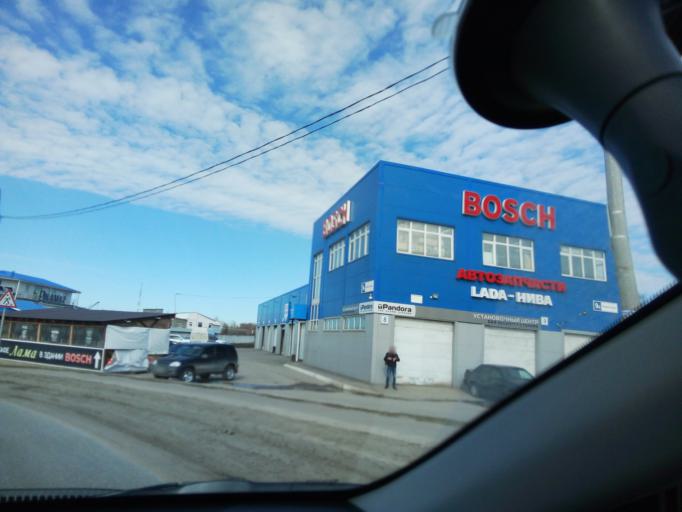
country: RU
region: Chuvashia
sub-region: Cheboksarskiy Rayon
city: Cheboksary
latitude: 56.1022
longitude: 47.2529
